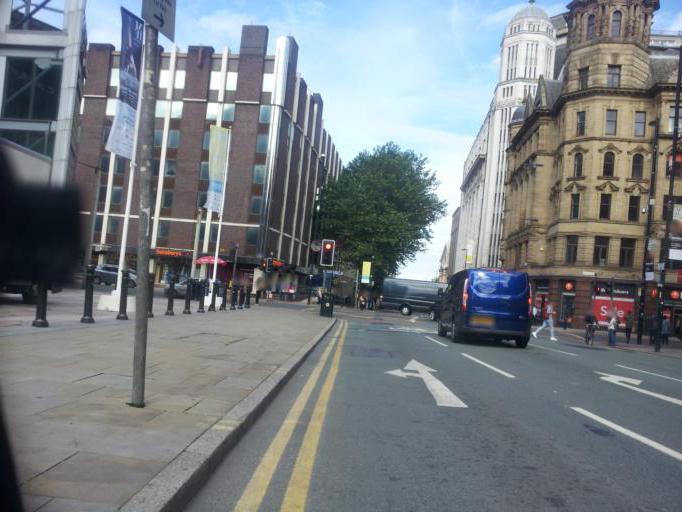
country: GB
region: England
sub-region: Manchester
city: Manchester
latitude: 53.4783
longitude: -2.2490
